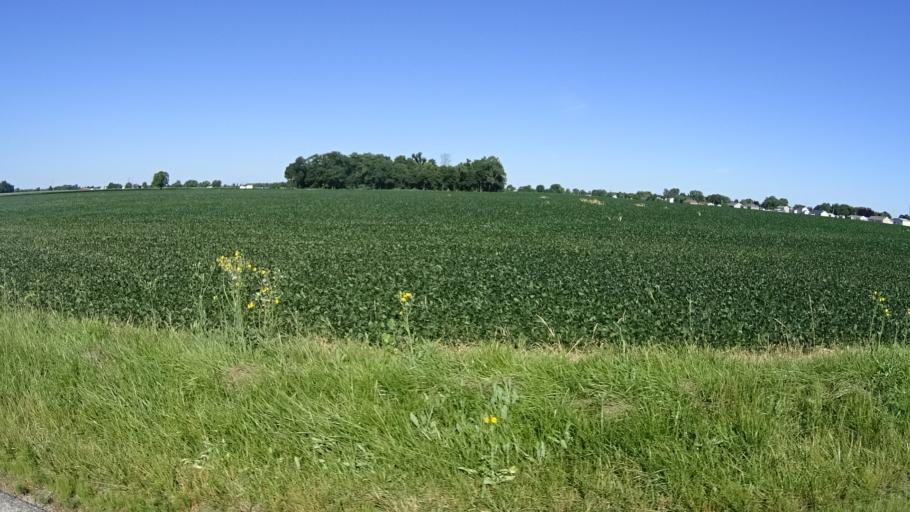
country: US
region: Ohio
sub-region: Erie County
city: Sandusky
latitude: 41.3925
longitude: -82.7194
